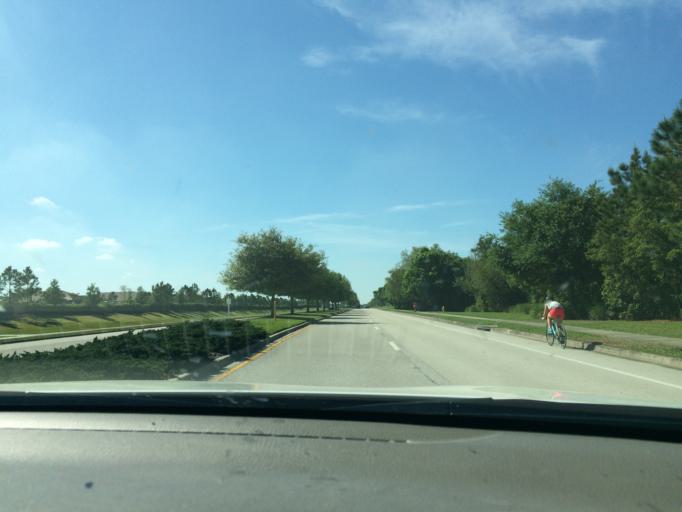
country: US
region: Florida
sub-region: Sarasota County
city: The Meadows
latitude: 27.4150
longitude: -82.3995
